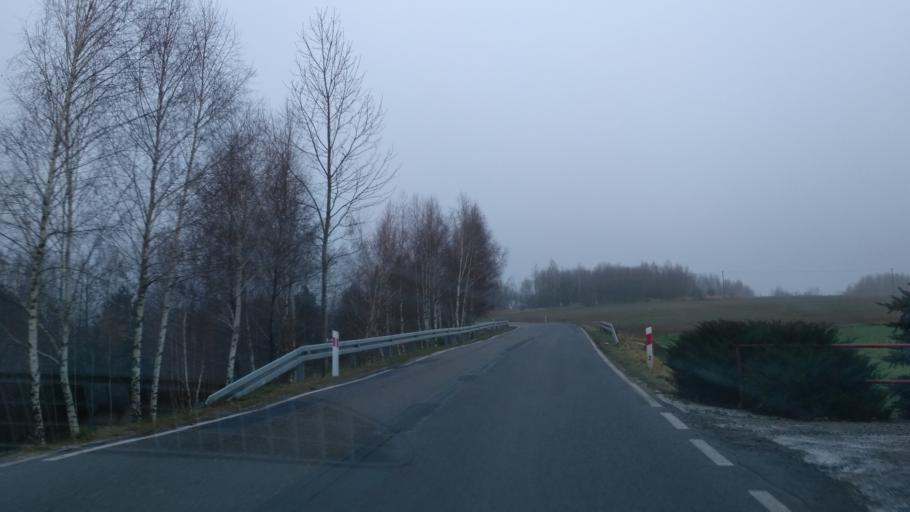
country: PL
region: Subcarpathian Voivodeship
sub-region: Powiat lancucki
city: Handzlowka
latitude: 49.9665
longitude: 22.1914
